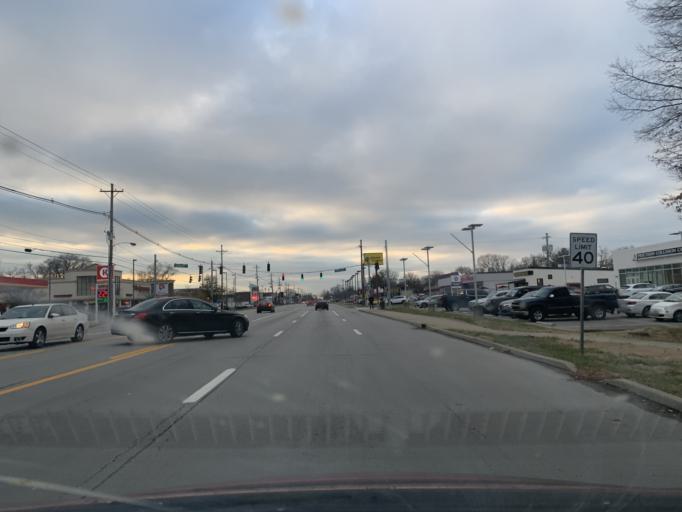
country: US
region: Kentucky
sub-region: Jefferson County
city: Beechwood Village
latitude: 38.2513
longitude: -85.6353
